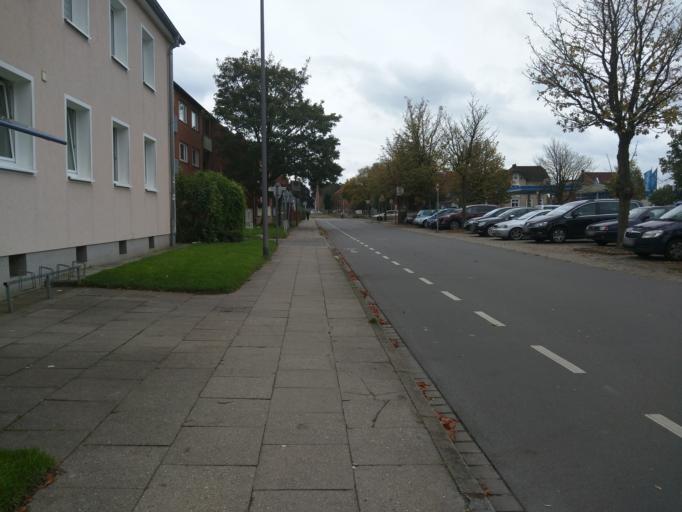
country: DE
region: Schleswig-Holstein
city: Lauenburg
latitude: 53.3750
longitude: 10.5509
